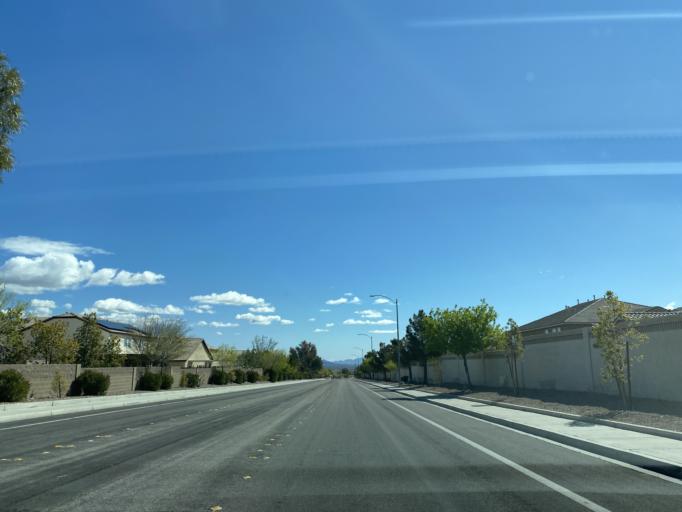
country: US
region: Nevada
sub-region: Clark County
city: Summerlin South
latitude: 36.3250
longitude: -115.2924
